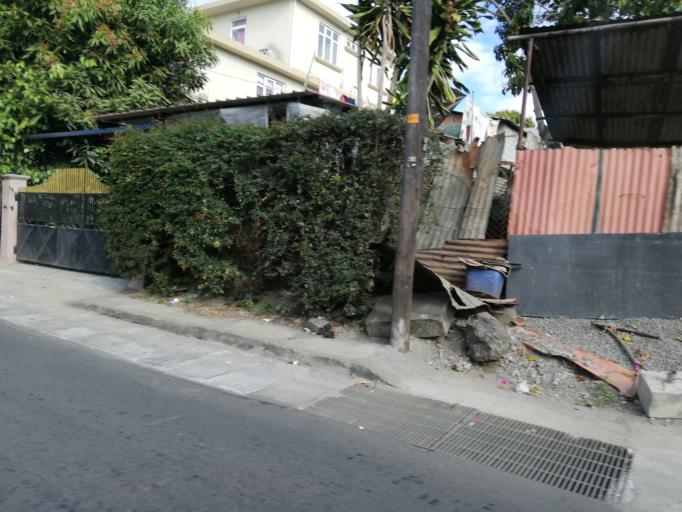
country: MU
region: Black River
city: Gros Cailloux
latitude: -20.2313
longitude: 57.4562
